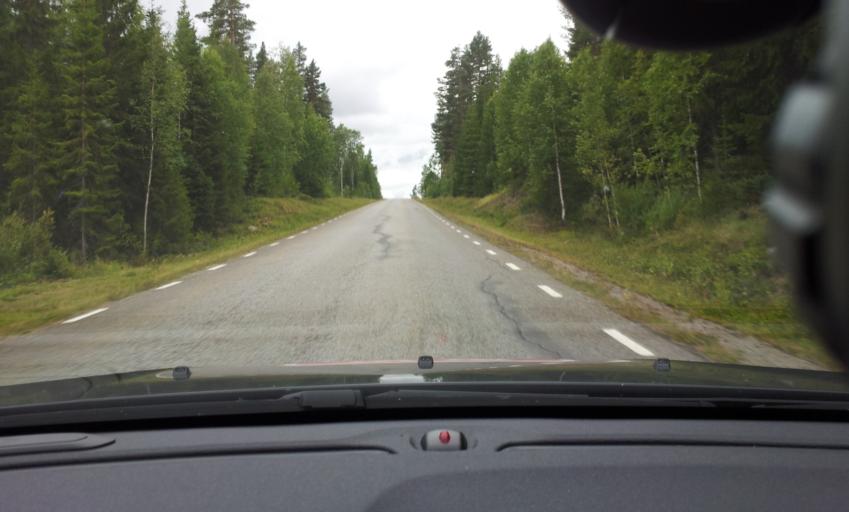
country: SE
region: Jaemtland
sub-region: OEstersunds Kommun
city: Brunflo
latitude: 62.9593
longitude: 15.1110
